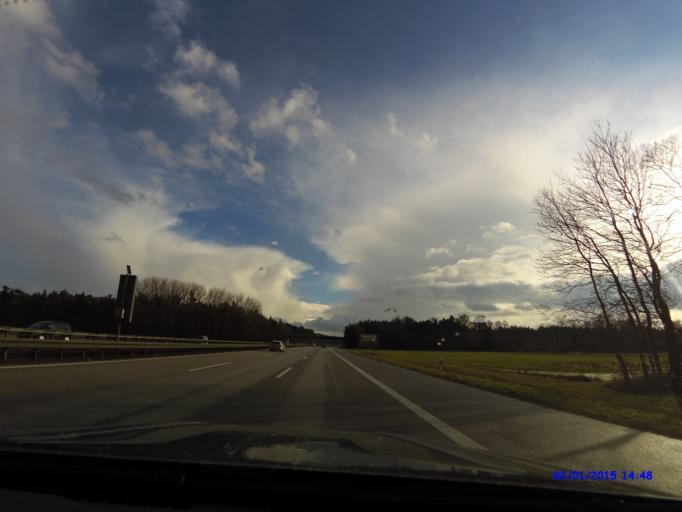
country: DE
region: Bavaria
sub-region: Upper Bavaria
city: Reichertshofen
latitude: 48.6729
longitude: 11.5061
